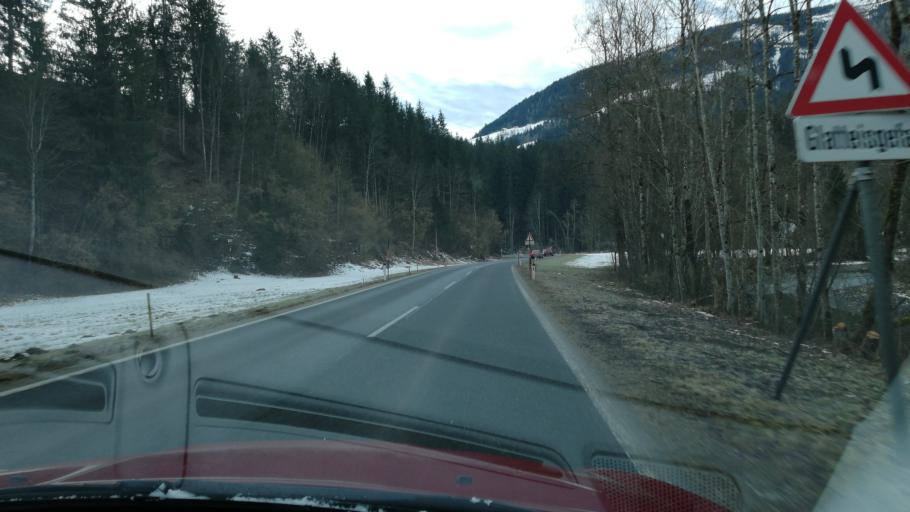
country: AT
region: Styria
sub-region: Politischer Bezirk Liezen
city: Irdning
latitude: 47.4880
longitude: 14.1085
